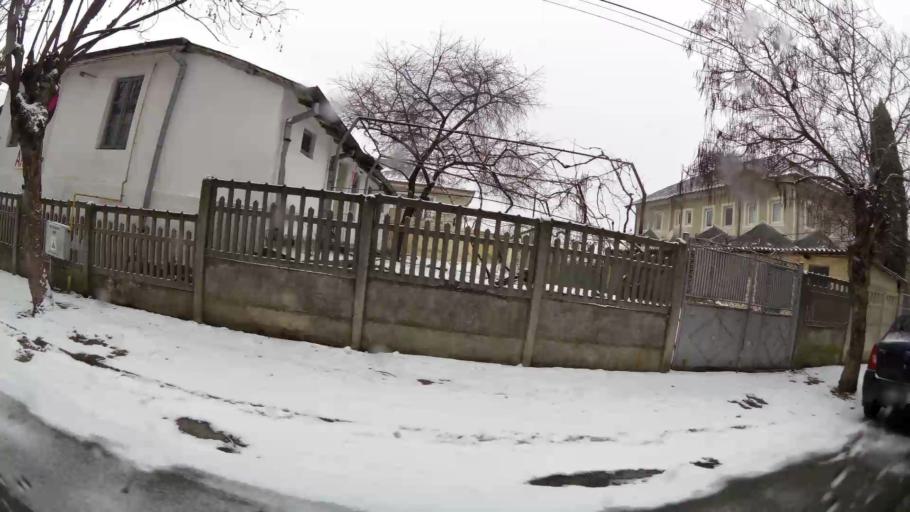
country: RO
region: Dambovita
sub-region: Municipiul Targoviste
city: Targoviste
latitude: 44.9336
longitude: 25.4521
